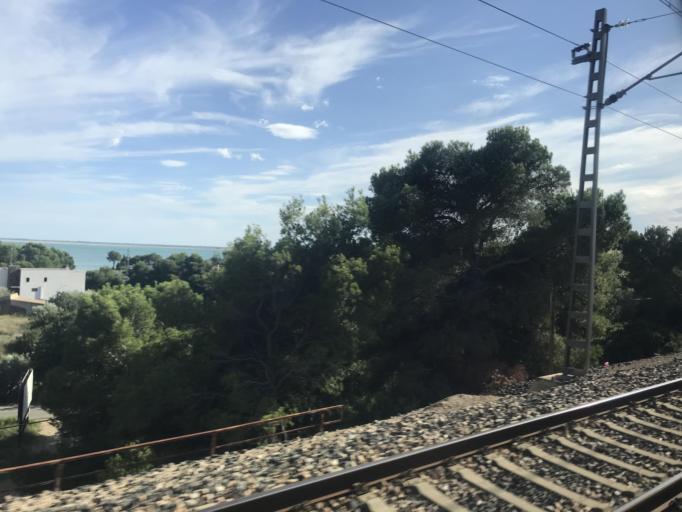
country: ES
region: Catalonia
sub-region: Provincia de Tarragona
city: L'Ampolla
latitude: 40.8277
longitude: 0.7343
